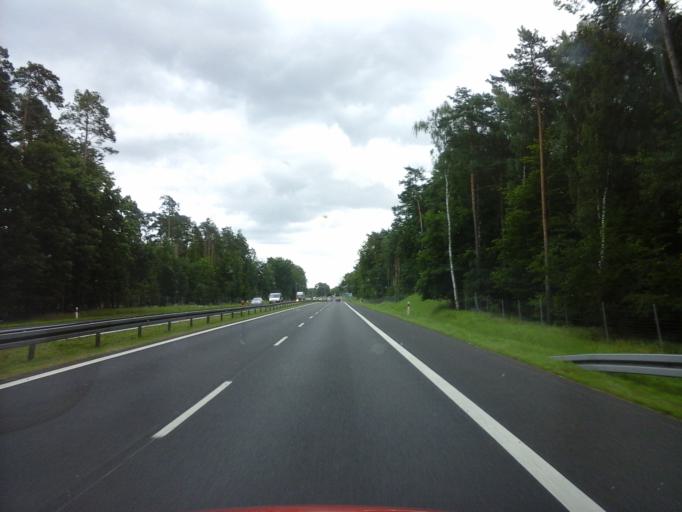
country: PL
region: West Pomeranian Voivodeship
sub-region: Powiat stargardzki
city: Kobylanka
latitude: 53.3504
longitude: 14.8263
